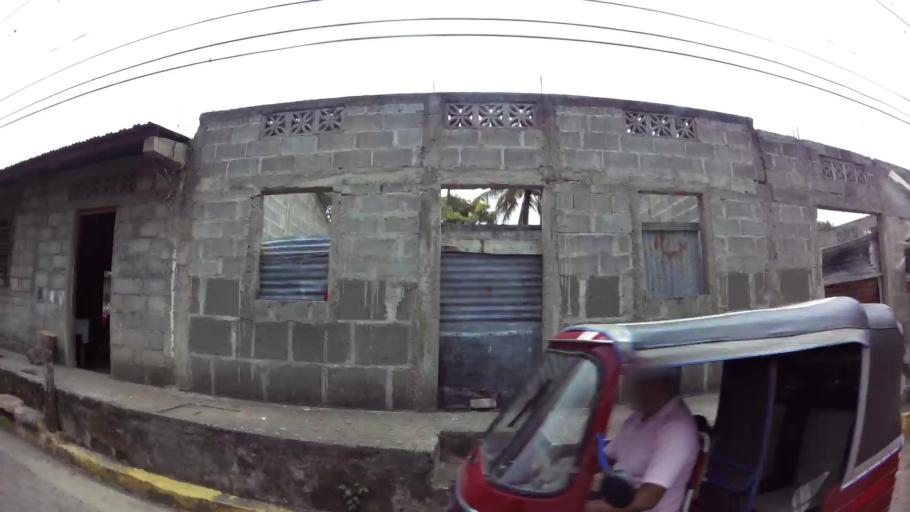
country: NI
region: Granada
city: Diriomo
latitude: 11.8756
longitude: -86.0518
